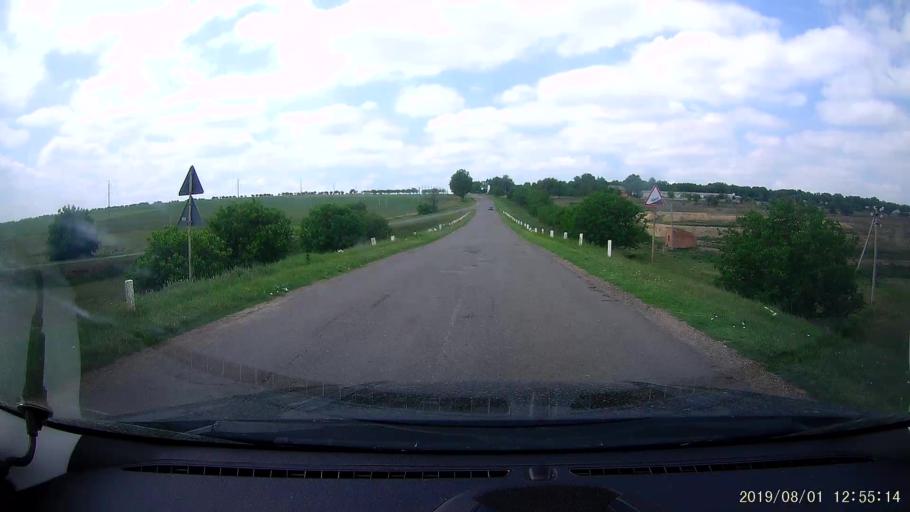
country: MD
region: Gagauzia
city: Vulcanesti
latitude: 45.6939
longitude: 28.4709
